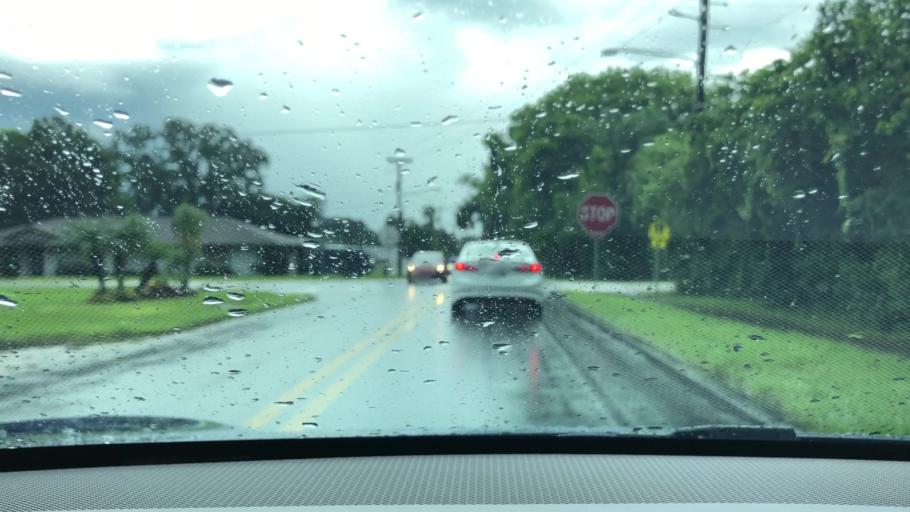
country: US
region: Florida
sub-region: Orange County
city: Edgewood
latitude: 28.4949
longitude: -81.3601
